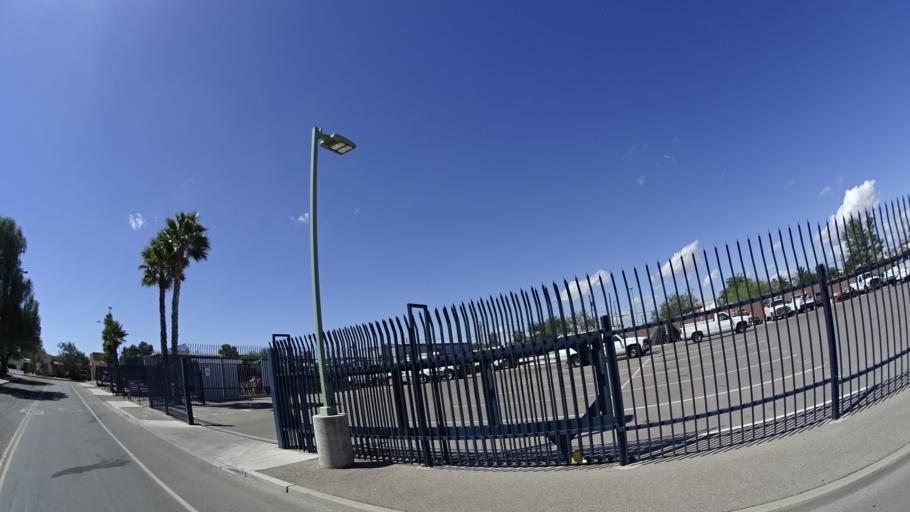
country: US
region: Arizona
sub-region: Pima County
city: Tucson
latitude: 32.2403
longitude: -110.9491
